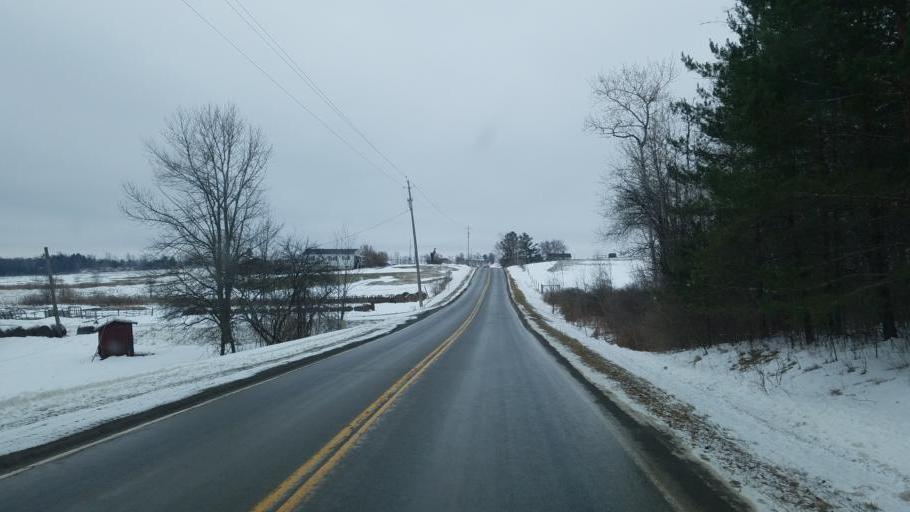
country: US
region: Pennsylvania
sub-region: Tioga County
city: Elkland
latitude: 42.1058
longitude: -77.4095
